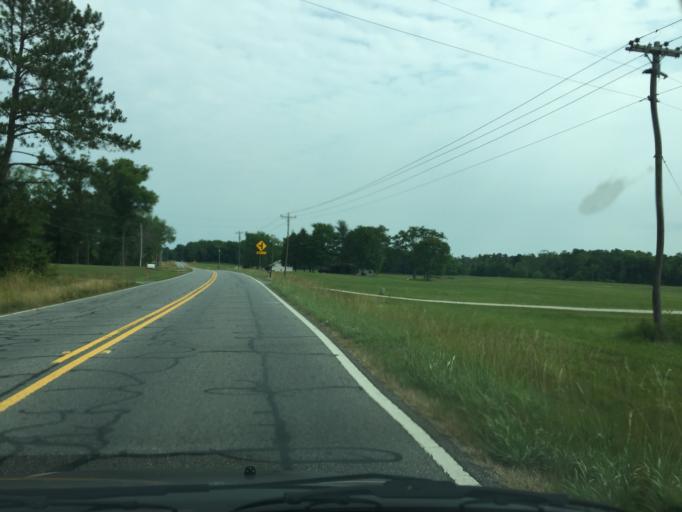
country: US
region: Georgia
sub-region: Catoosa County
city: Ringgold
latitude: 34.8531
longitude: -85.1427
